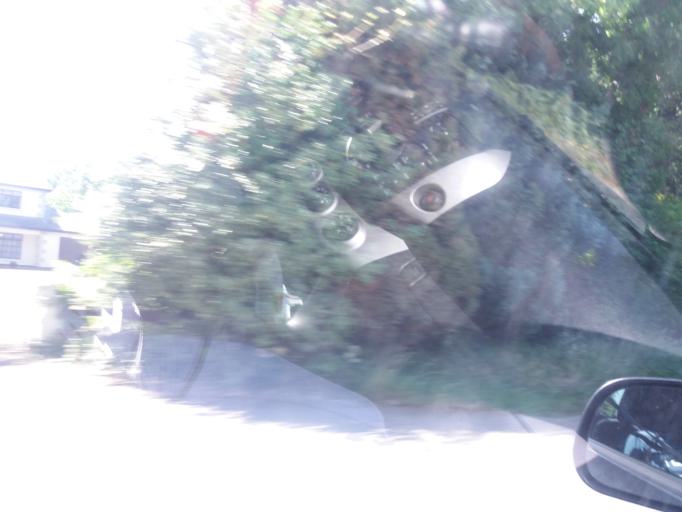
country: IE
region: Leinster
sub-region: An Mhi
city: Ashbourne
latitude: 53.5268
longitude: -6.2992
